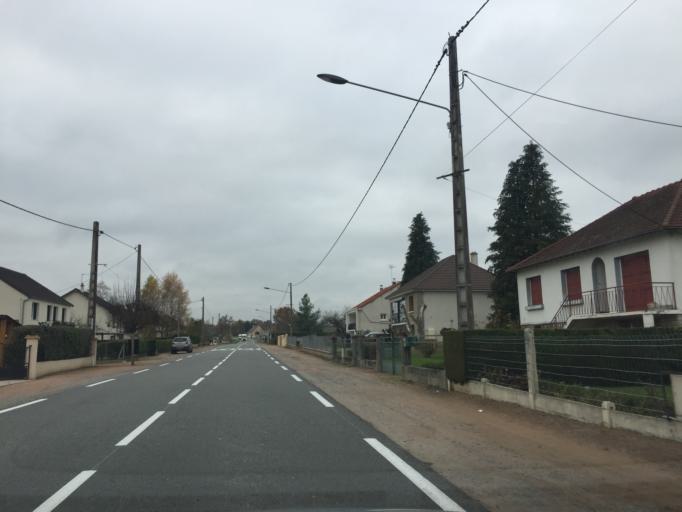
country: FR
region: Limousin
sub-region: Departement de la Creuse
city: Gouzon
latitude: 46.1863
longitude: 2.2341
